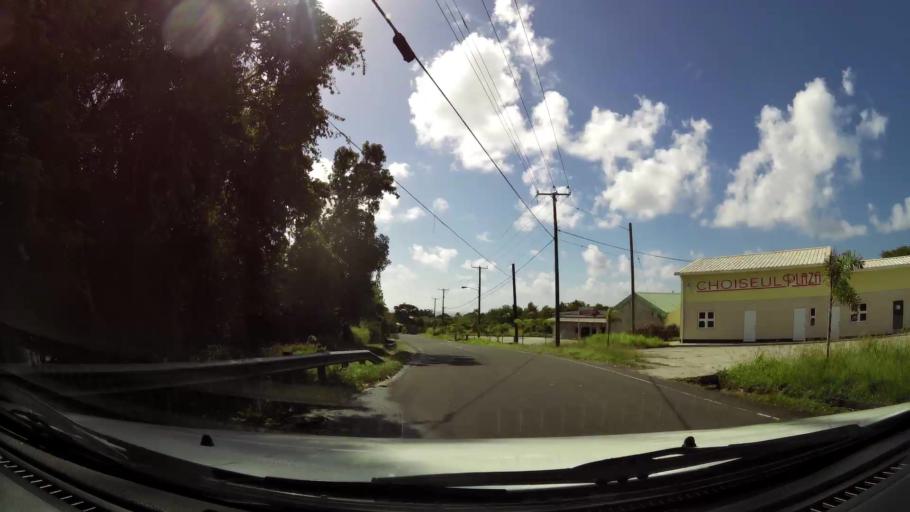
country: LC
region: Choiseul Quarter
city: Choiseul
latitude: 13.7748
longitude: -61.0318
